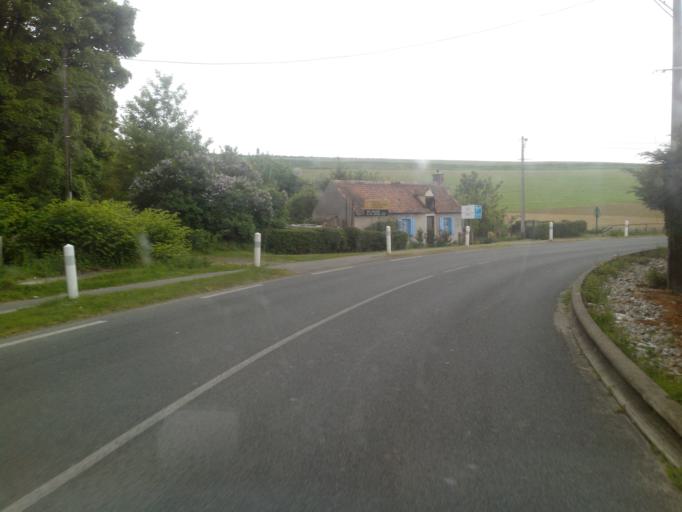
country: FR
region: Nord-Pas-de-Calais
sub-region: Departement du Pas-de-Calais
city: Condette
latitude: 50.6675
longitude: 1.6357
